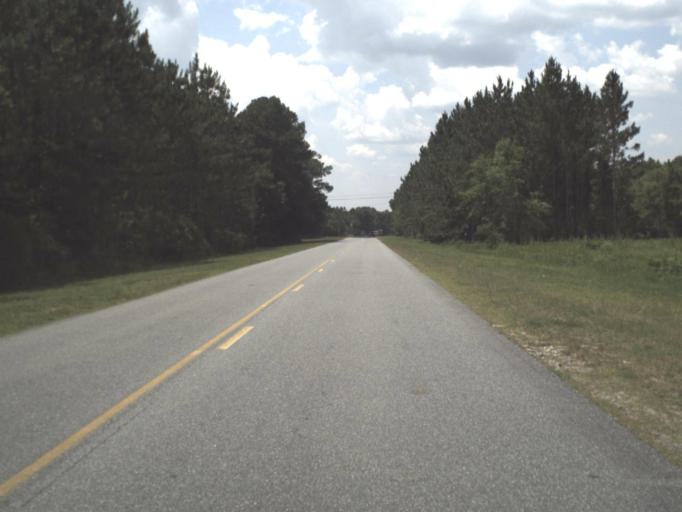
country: US
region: Florida
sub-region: Bradford County
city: Starke
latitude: 30.0246
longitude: -82.0538
